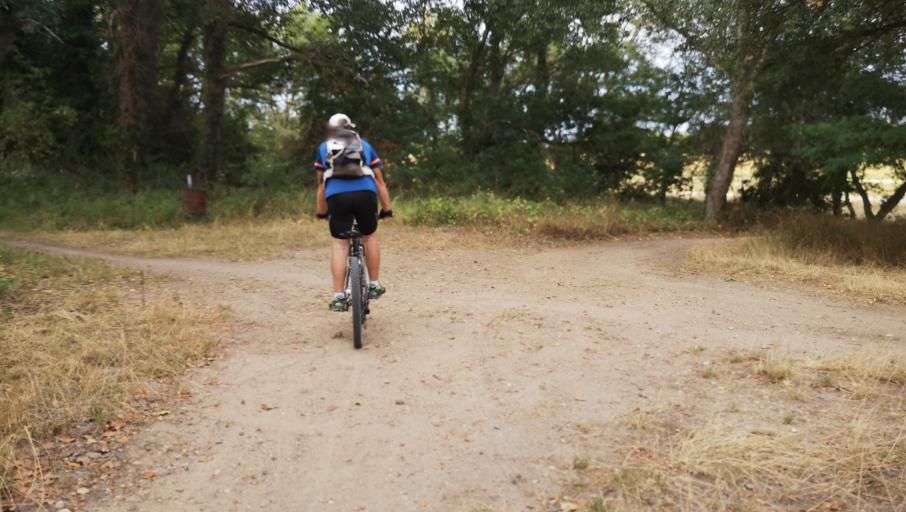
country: FR
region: Centre
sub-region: Departement du Loiret
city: Sandillon
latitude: 47.8585
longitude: 2.0352
